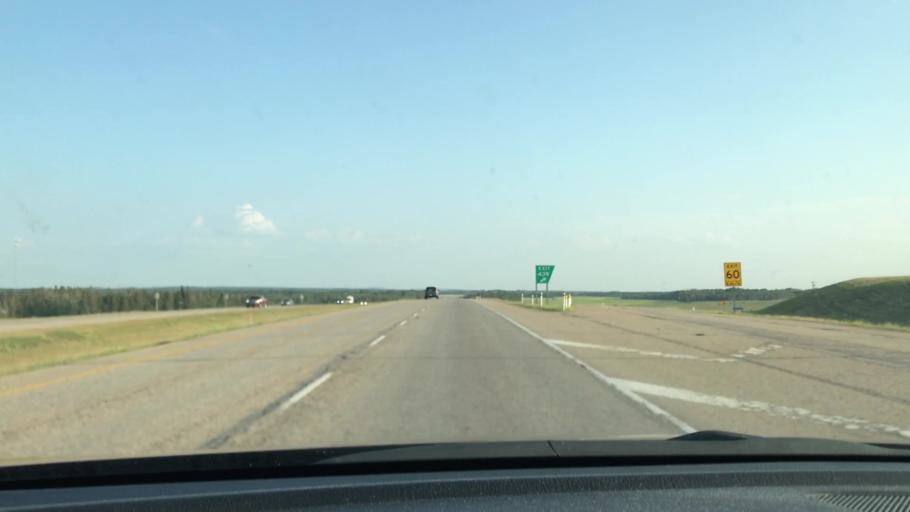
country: CA
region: Alberta
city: Ponoka
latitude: 52.5825
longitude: -113.6632
